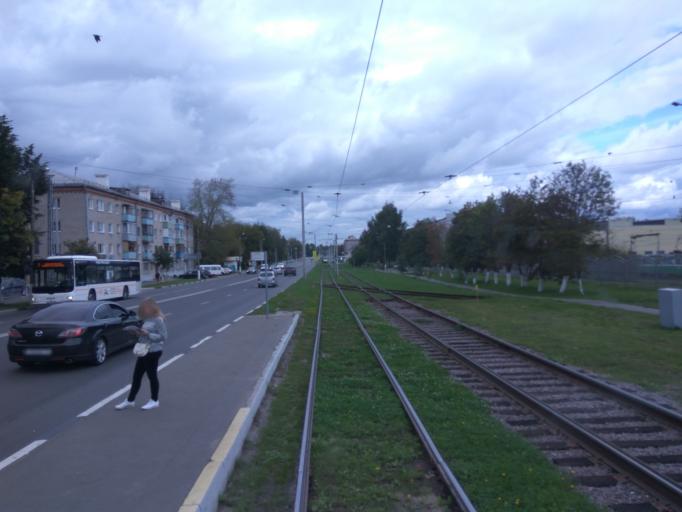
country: RU
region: Moskovskaya
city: Kolomna
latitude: 55.0879
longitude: 38.7657
